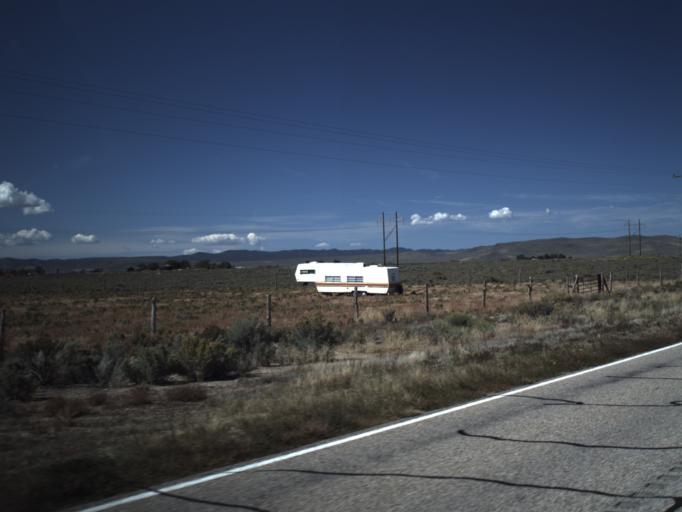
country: US
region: Utah
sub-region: Washington County
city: Enterprise
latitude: 37.7038
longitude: -113.6404
